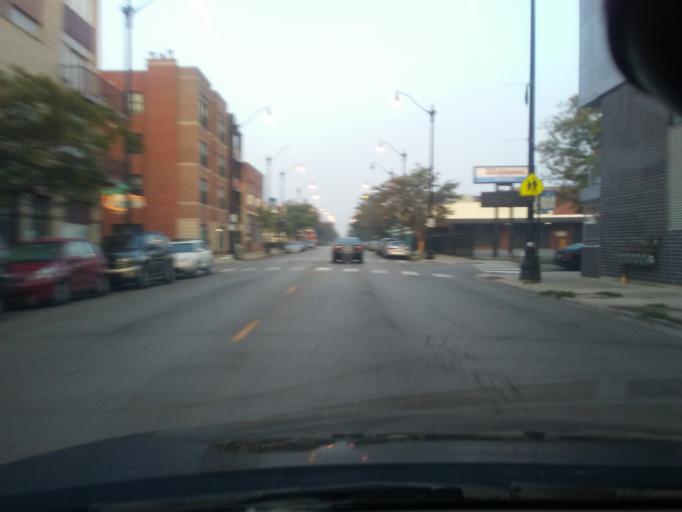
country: US
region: Illinois
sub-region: Cook County
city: Chicago
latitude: 41.9180
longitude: -87.7040
